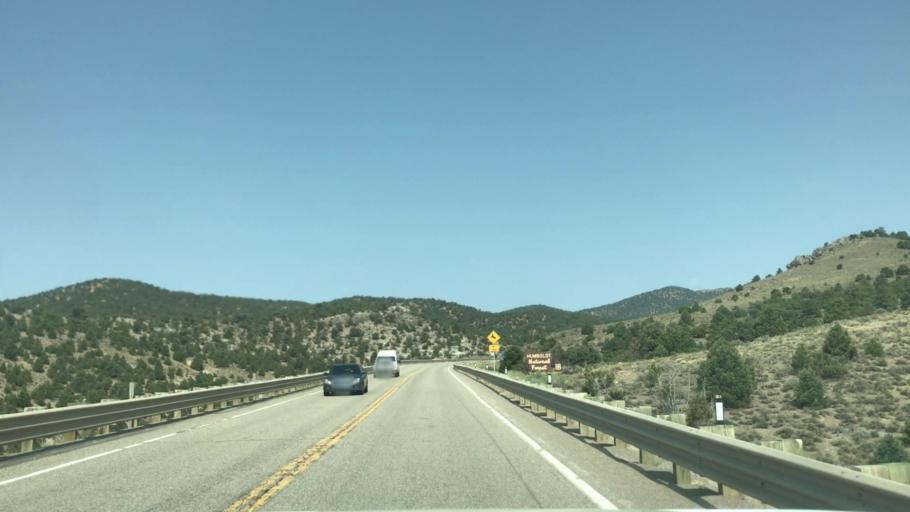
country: US
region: Nevada
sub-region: White Pine County
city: Ely
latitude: 39.0339
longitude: -114.6031
